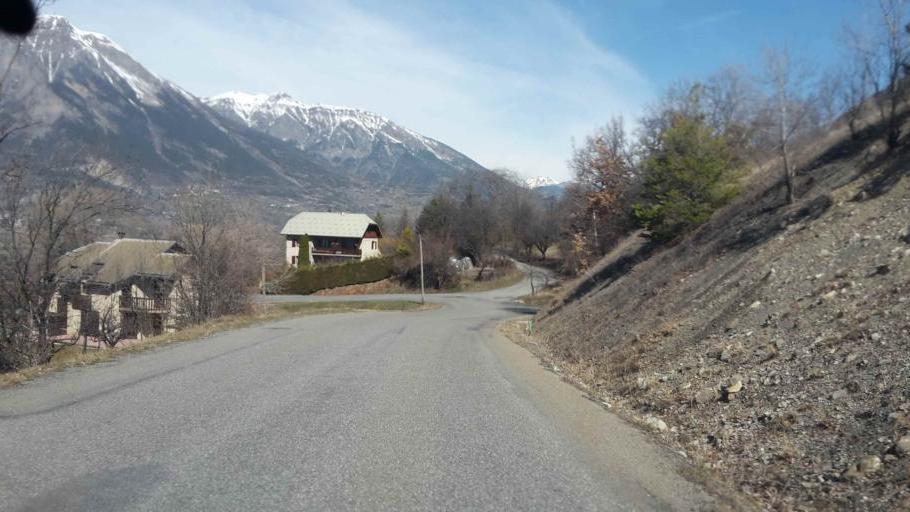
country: FR
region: Provence-Alpes-Cote d'Azur
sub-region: Departement des Hautes-Alpes
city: Embrun
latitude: 44.5797
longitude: 6.5329
